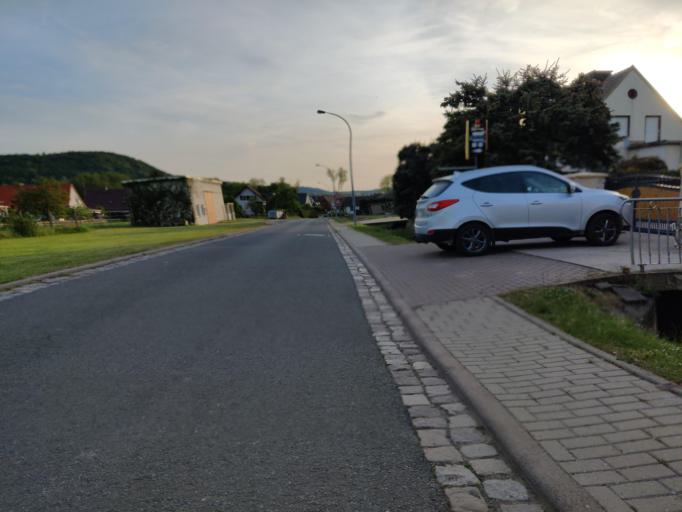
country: DE
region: Saxony-Anhalt
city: Balgstadt
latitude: 51.2218
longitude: 11.7083
